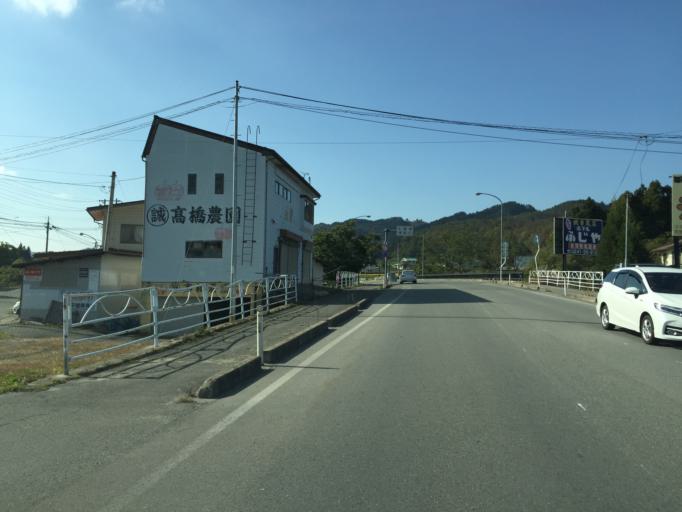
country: JP
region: Yamagata
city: Yonezawa
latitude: 37.9140
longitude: 140.0700
